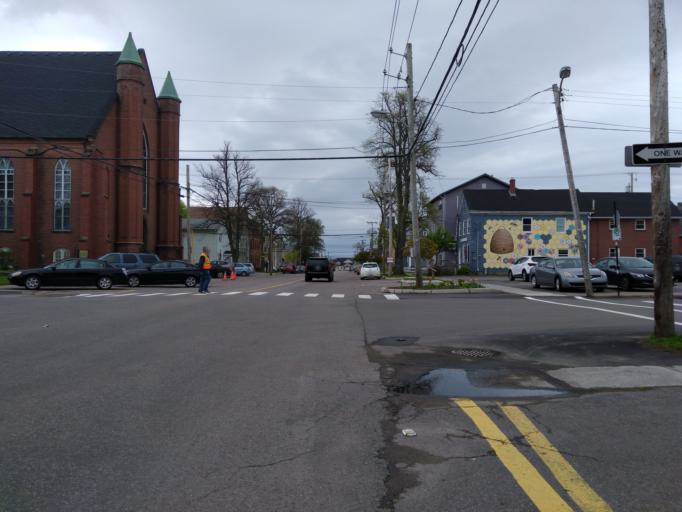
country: CA
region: Prince Edward Island
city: Charlottetown
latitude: 46.2357
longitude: -63.1243
